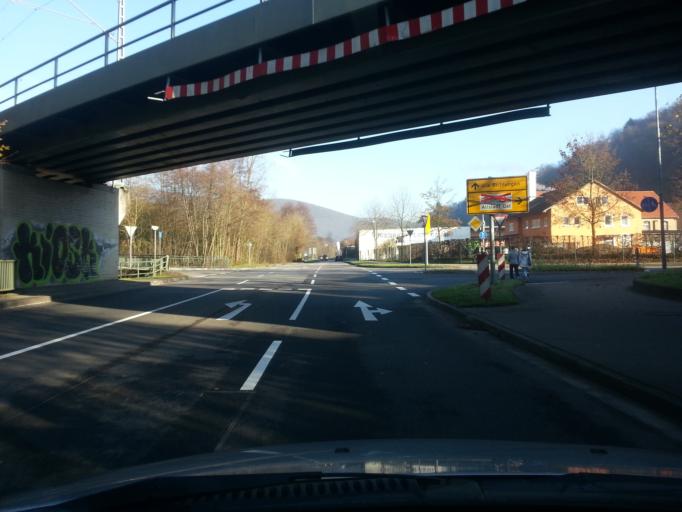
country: DE
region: Baden-Wuerttemberg
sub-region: Karlsruhe Region
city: Eberbach
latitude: 49.4679
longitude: 8.9811
